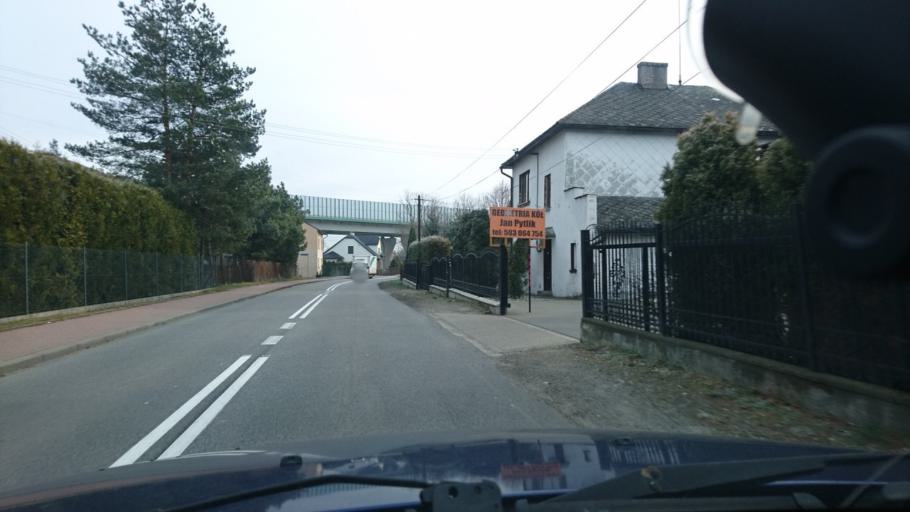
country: PL
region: Silesian Voivodeship
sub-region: Powiat bielski
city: Rybarzowice
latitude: 49.7284
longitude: 19.1153
